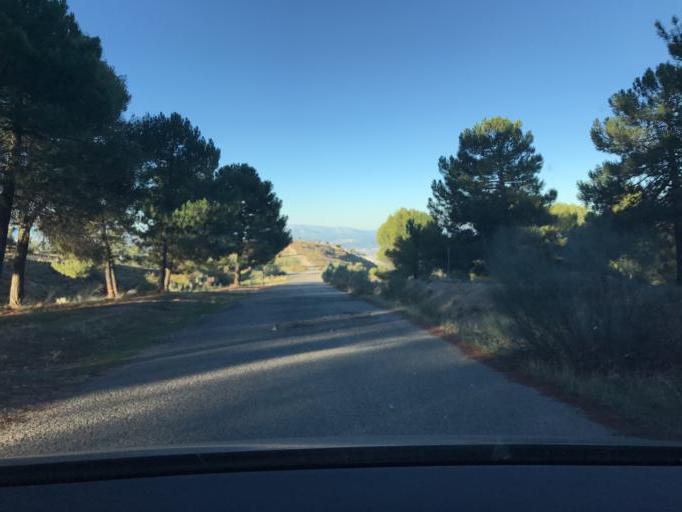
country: ES
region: Andalusia
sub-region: Provincia de Granada
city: Viznar
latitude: 37.2353
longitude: -3.5455
